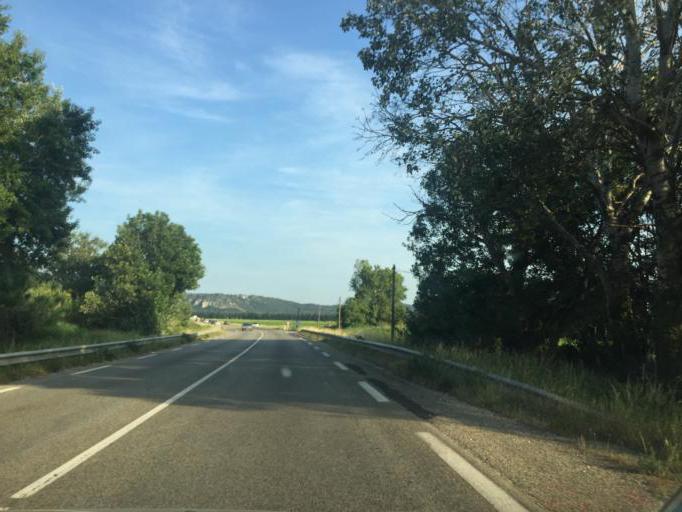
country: FR
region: Languedoc-Roussillon
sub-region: Departement du Gard
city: Pujaut
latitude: 43.9963
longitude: 4.7391
